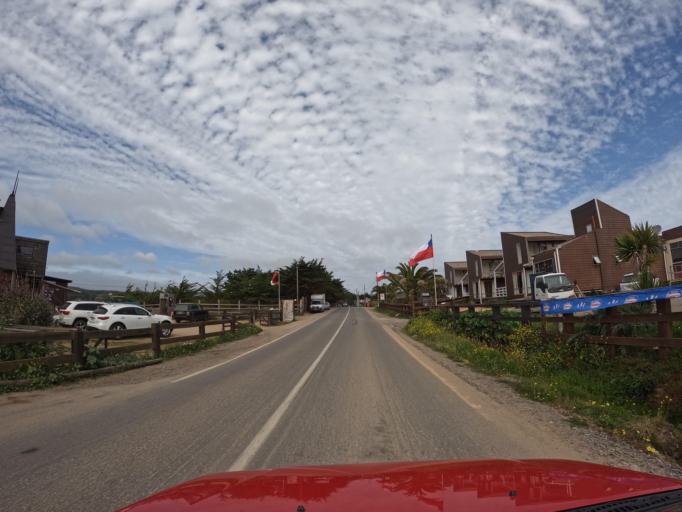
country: CL
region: O'Higgins
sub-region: Provincia de Colchagua
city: Santa Cruz
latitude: -34.4286
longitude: -72.0410
